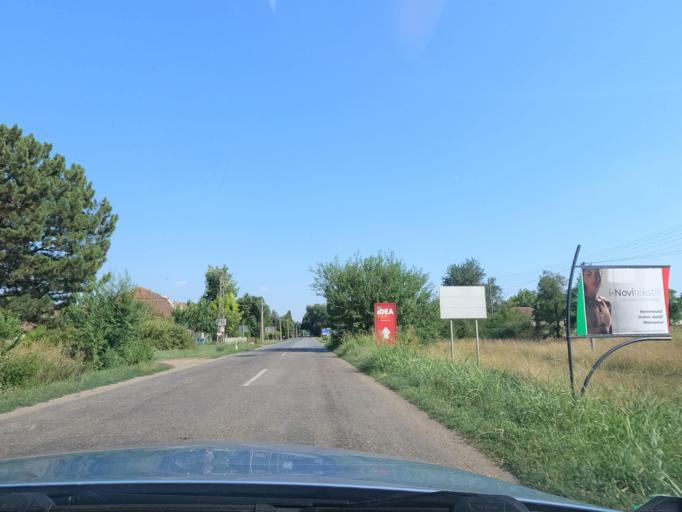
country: RS
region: Autonomna Pokrajina Vojvodina
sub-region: Juznobacki Okrug
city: Becej
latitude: 45.6312
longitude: 20.0162
